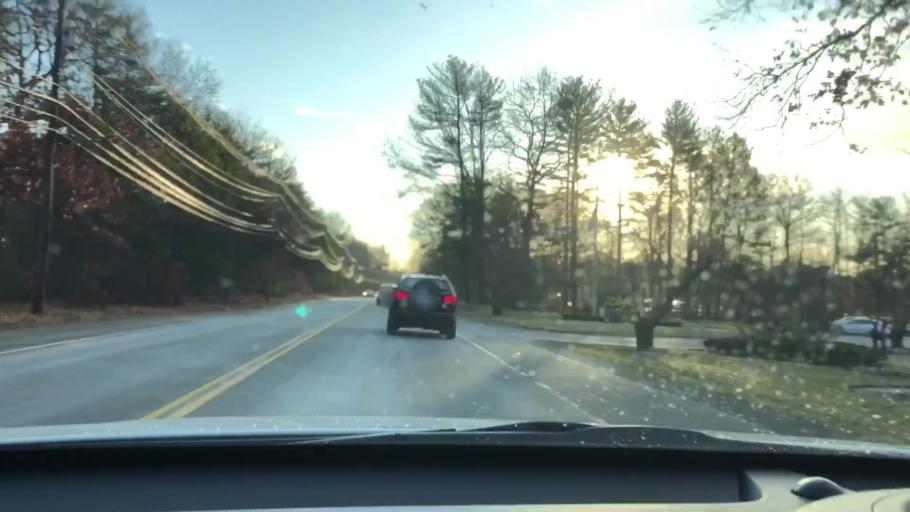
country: US
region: Massachusetts
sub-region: Plymouth County
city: Rockland
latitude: 42.1627
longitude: -70.8862
